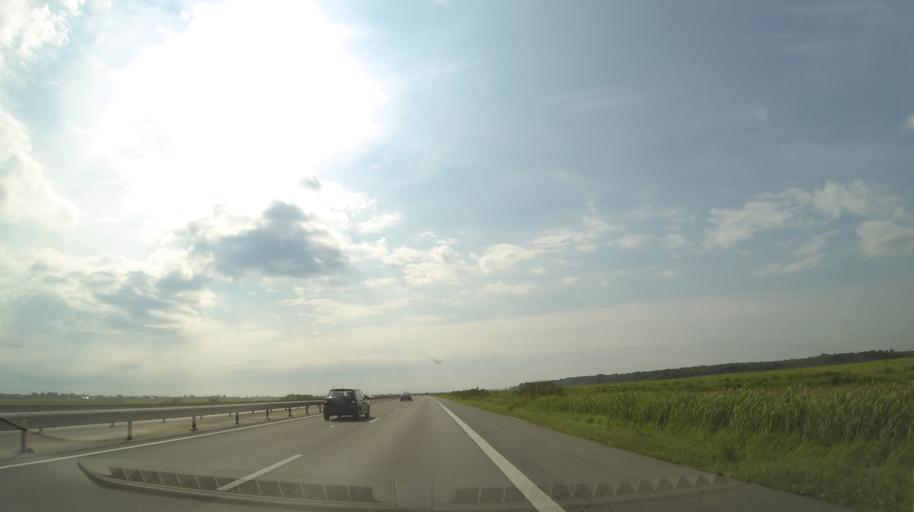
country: RO
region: Dambovita
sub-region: Comuna Corbii Mari
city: Grozavesti
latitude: 44.5760
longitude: 25.4748
